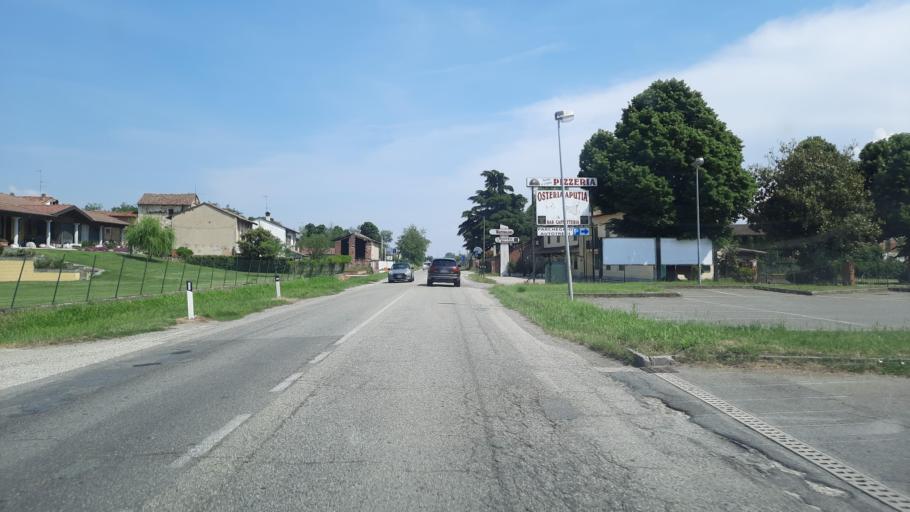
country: IT
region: Lombardy
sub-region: Provincia di Pavia
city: Villanova d'Ardenghi
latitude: 45.1652
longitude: 9.0173
